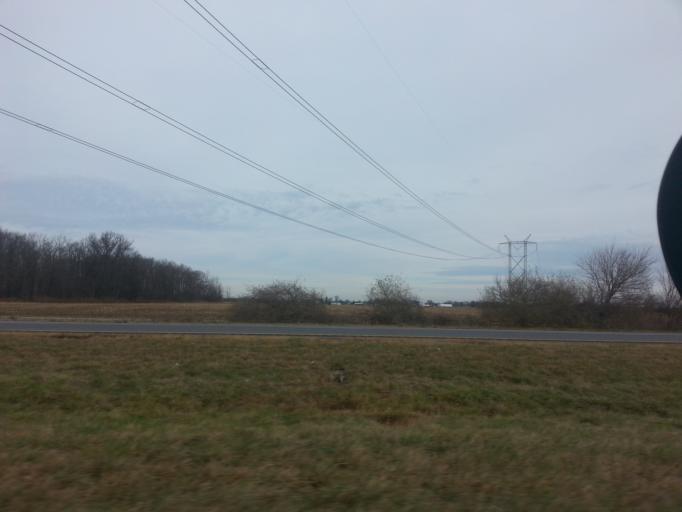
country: US
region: Indiana
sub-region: Hendricks County
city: Pittsboro
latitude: 39.8794
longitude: -86.4838
